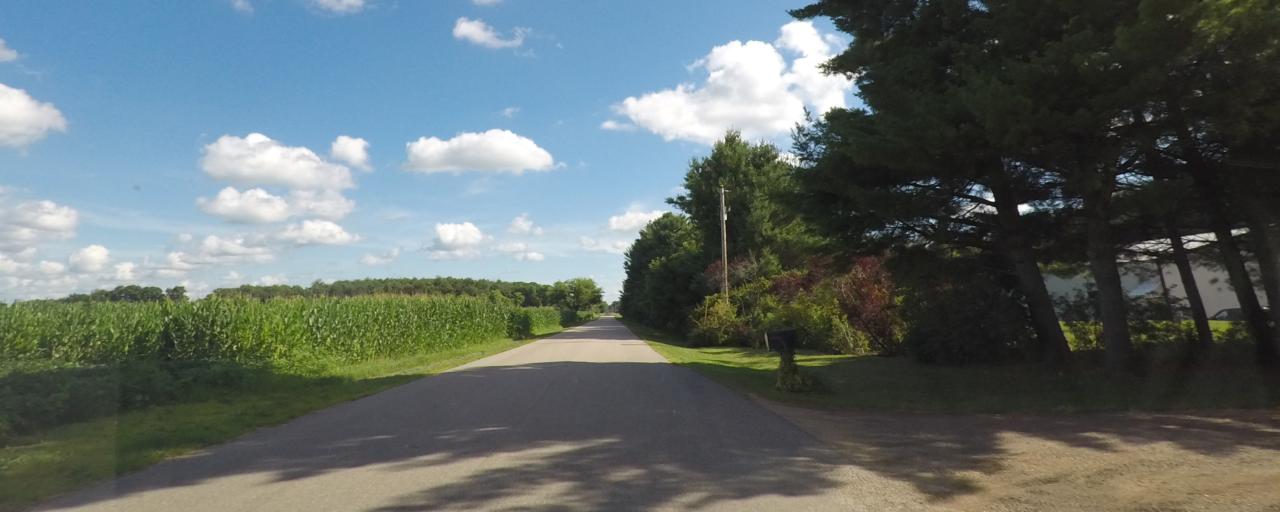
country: US
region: Wisconsin
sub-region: Rock County
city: Edgerton
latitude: 42.8944
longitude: -89.1320
